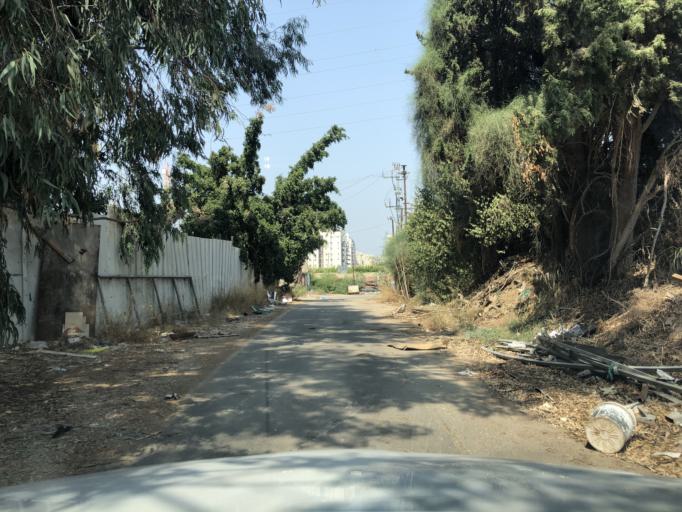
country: IL
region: Central District
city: Ganne Tiqwa
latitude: 32.0698
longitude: 34.8759
